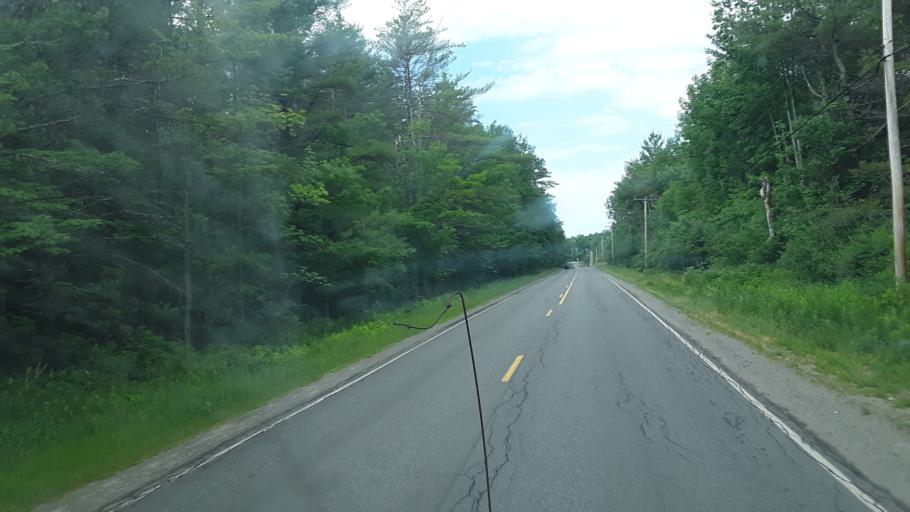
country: US
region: Maine
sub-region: Penobscot County
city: Hampden
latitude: 44.7308
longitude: -68.8655
